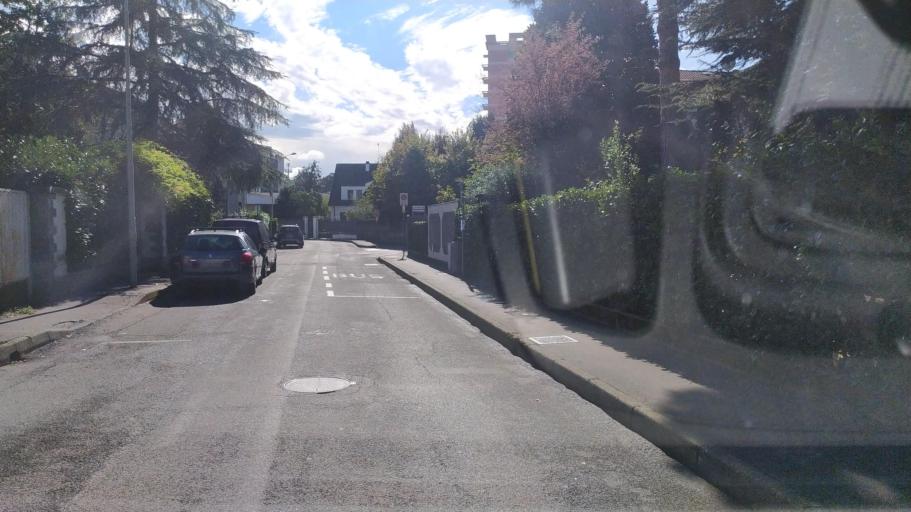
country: IT
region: Lombardy
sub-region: Citta metropolitana di Milano
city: Trezzano sul Naviglio
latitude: 45.4255
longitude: 9.0608
